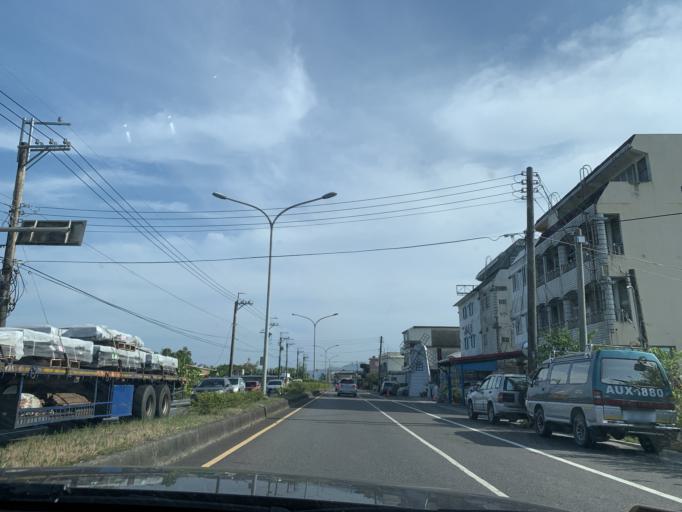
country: TW
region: Taiwan
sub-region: Yilan
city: Yilan
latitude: 24.7511
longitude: 121.8159
